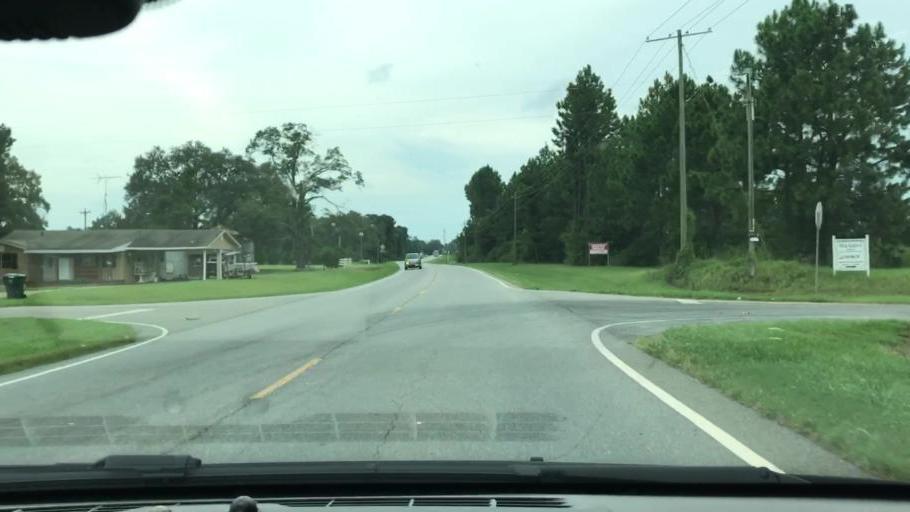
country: US
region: Georgia
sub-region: Early County
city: Blakely
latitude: 31.3827
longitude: -84.9573
